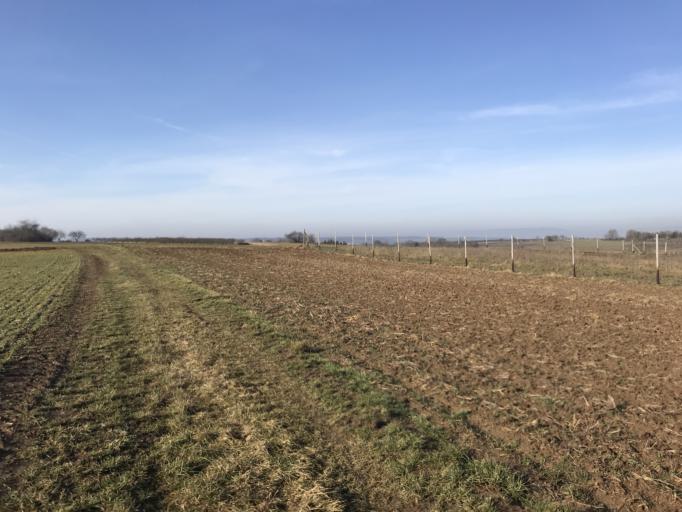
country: DE
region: Rheinland-Pfalz
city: Schwabenheim
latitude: 49.9481
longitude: 8.1064
